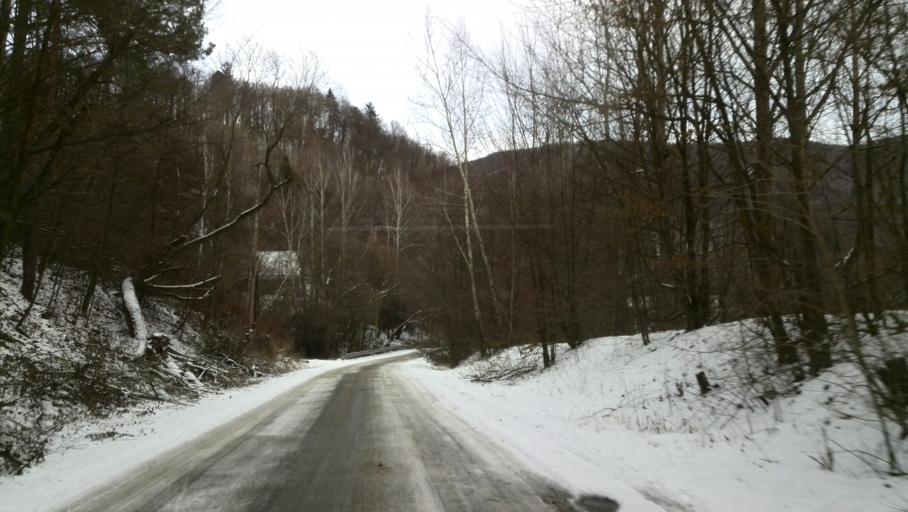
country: SK
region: Kosicky
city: Gelnica
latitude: 48.8297
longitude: 21.0712
